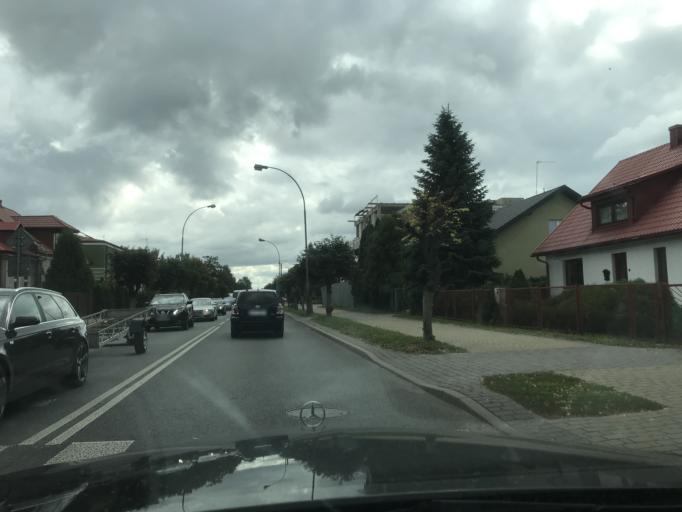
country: PL
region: Lublin Voivodeship
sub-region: Powiat janowski
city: Janow Lubelski
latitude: 50.7020
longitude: 22.4188
